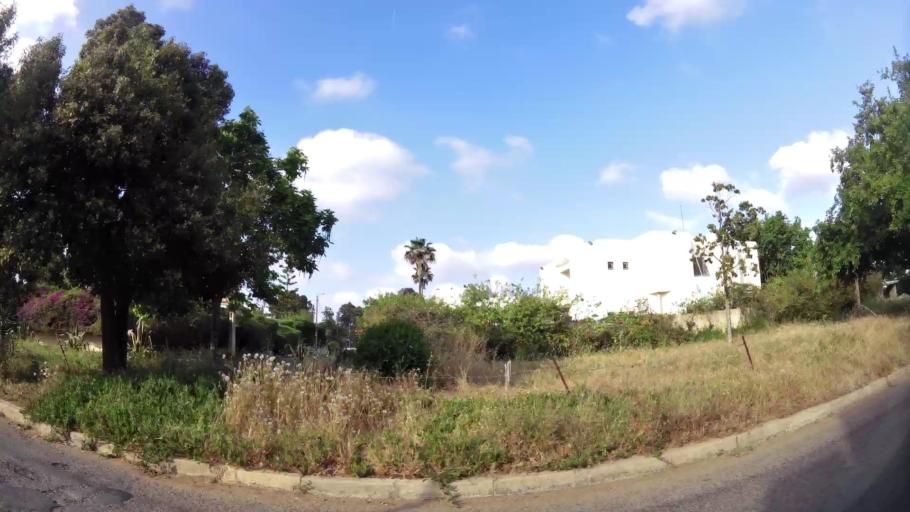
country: MA
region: Rabat-Sale-Zemmour-Zaer
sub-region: Skhirate-Temara
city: Temara
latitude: 33.9577
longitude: -6.8549
